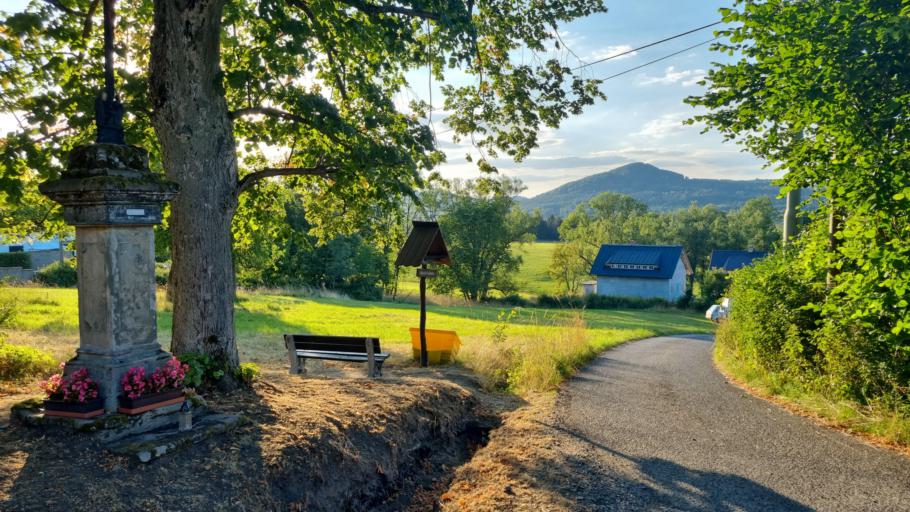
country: CZ
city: Novy Bor
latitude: 50.8070
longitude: 14.5273
